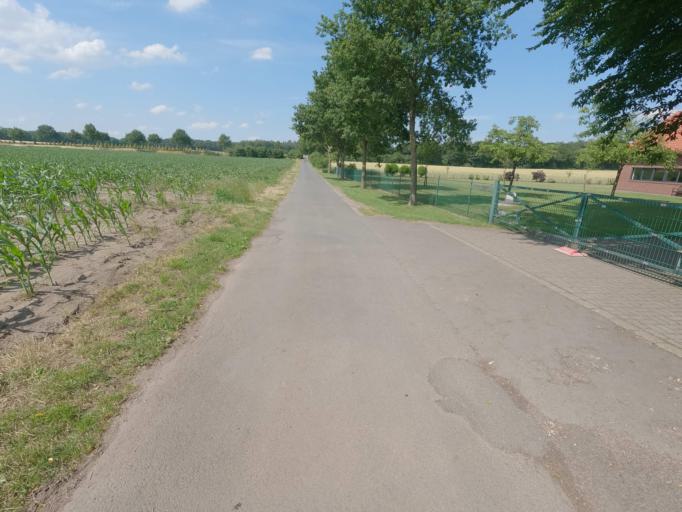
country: DE
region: North Rhine-Westphalia
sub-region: Regierungsbezirk Dusseldorf
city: Schermbeck
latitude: 51.6960
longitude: 6.8986
